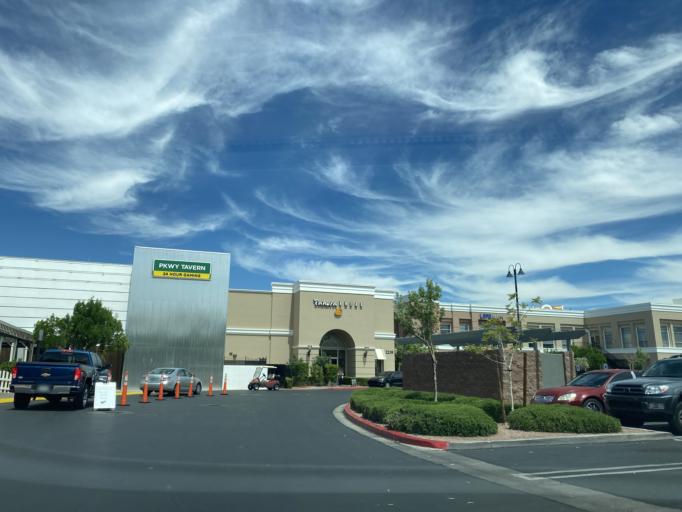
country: US
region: Nevada
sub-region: Clark County
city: Whitney
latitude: 36.0205
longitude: -115.0861
